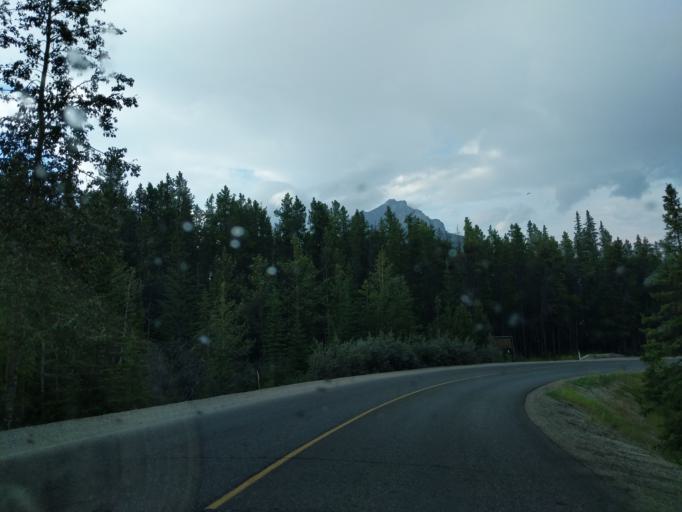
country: CA
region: Alberta
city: Banff
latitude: 51.1657
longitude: -115.5790
